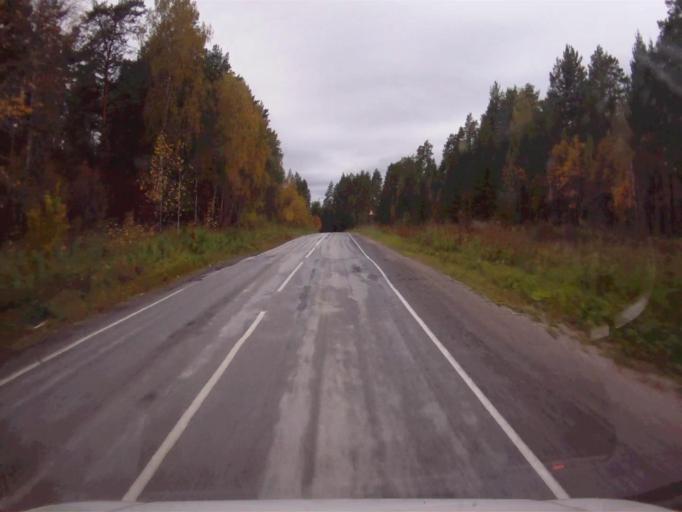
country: RU
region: Chelyabinsk
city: Nyazepetrovsk
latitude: 56.0557
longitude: 59.4736
